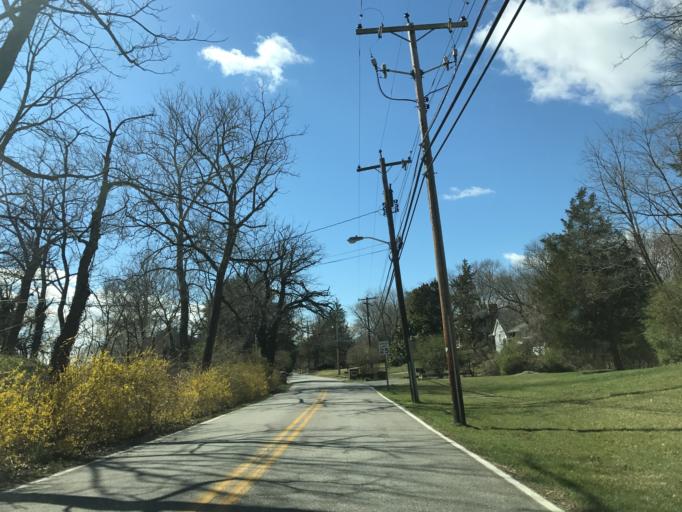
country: US
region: Maryland
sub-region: Anne Arundel County
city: Robinwood
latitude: 38.9508
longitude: -76.5276
